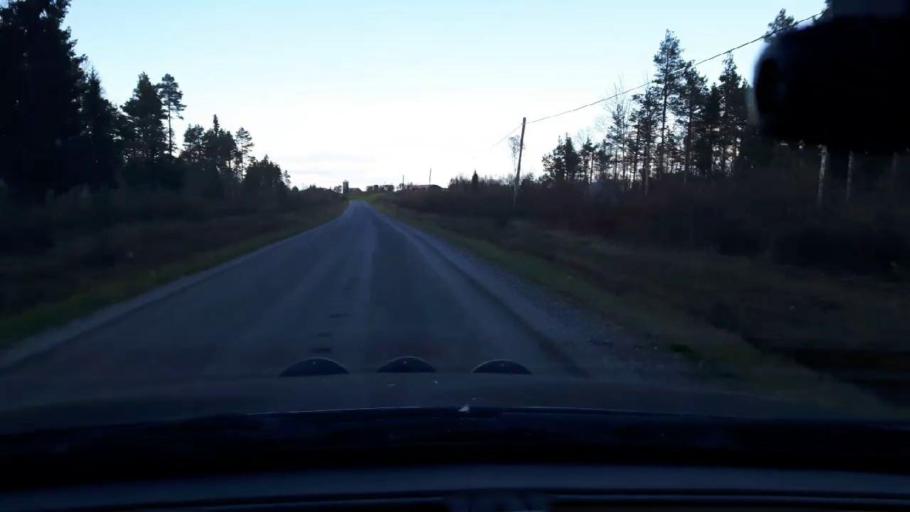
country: SE
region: Jaemtland
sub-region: Krokoms Kommun
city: Krokom
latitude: 63.0739
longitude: 14.2705
